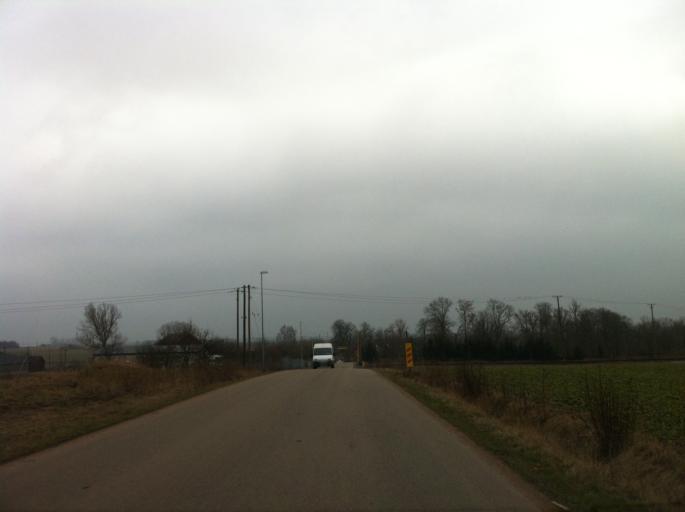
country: SE
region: Skane
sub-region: Landskrona
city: Asmundtorp
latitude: 55.9306
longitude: 13.0045
